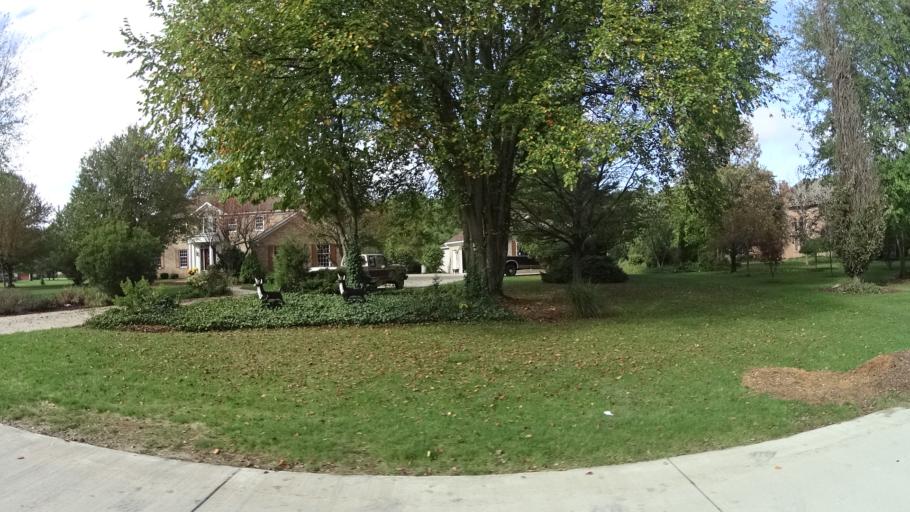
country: US
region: Ohio
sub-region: Lorain County
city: Eaton Estates
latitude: 41.3310
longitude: -82.0583
